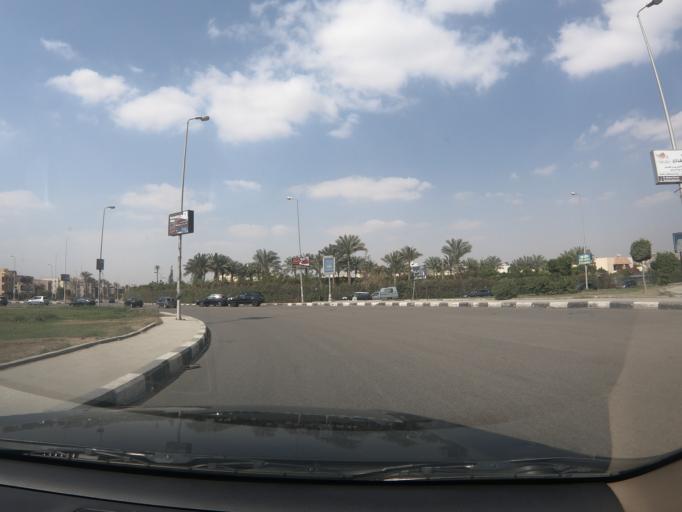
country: EG
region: Muhafazat al Qalyubiyah
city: Al Khankah
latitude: 30.0547
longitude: 31.4754
